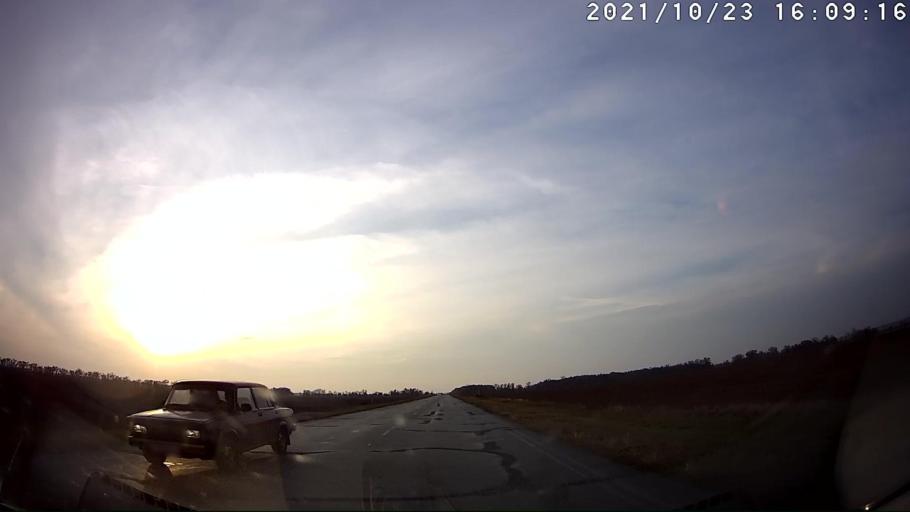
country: RU
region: Volgograd
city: Kotel'nikovo
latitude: 47.9439
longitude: 43.6990
